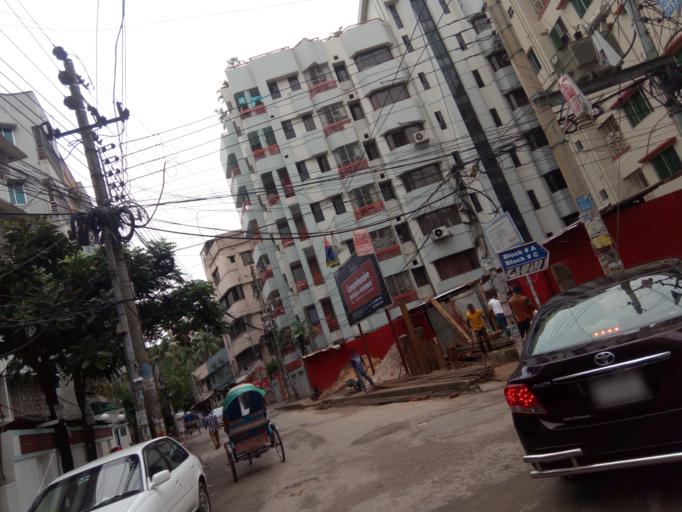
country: BD
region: Dhaka
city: Azimpur
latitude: 23.7564
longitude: 90.3725
